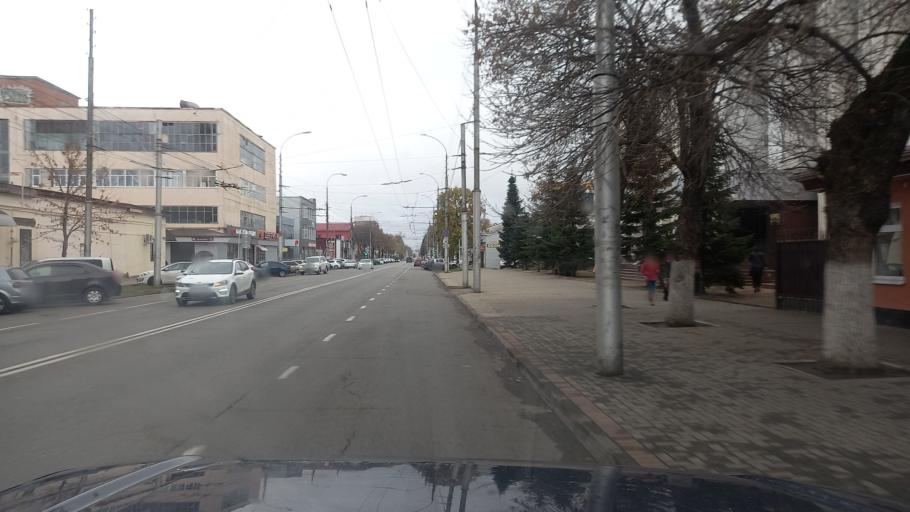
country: RU
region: Adygeya
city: Maykop
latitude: 44.6091
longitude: 40.1075
